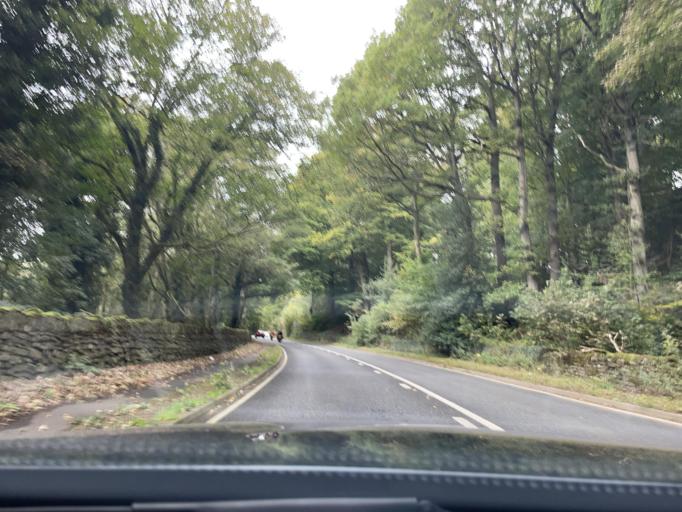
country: GB
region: England
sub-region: Sheffield
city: Bradfield
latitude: 53.3825
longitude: -1.5995
